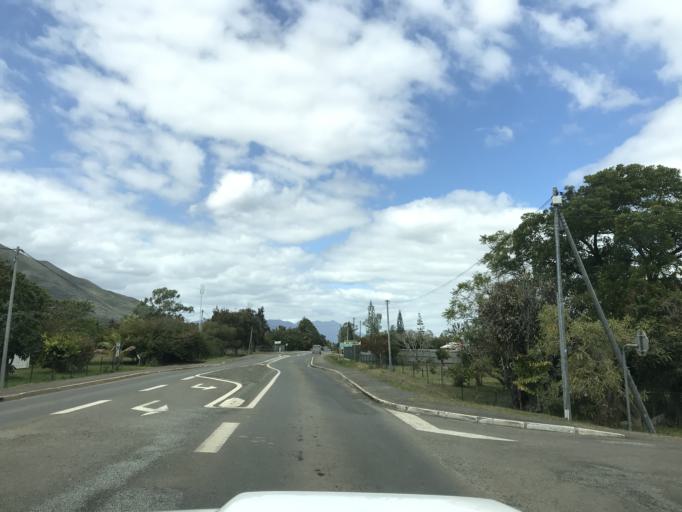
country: NC
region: South Province
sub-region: Bouloupari
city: Bouloupari
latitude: -21.9563
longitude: 166.1451
